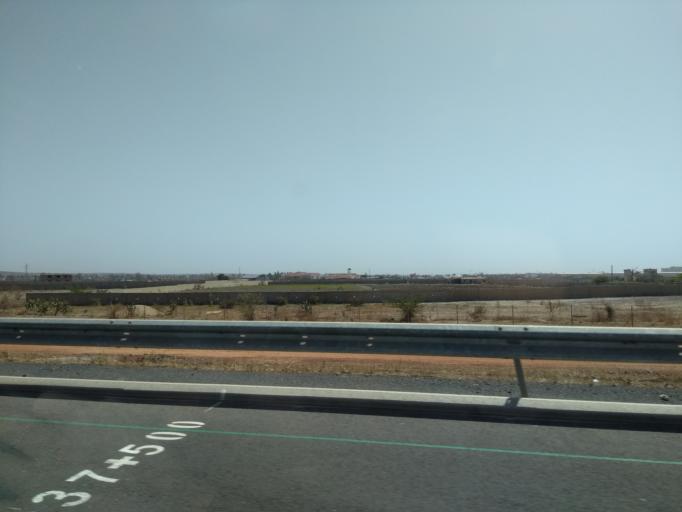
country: SN
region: Thies
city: Pout
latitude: 14.7343
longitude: -17.1630
